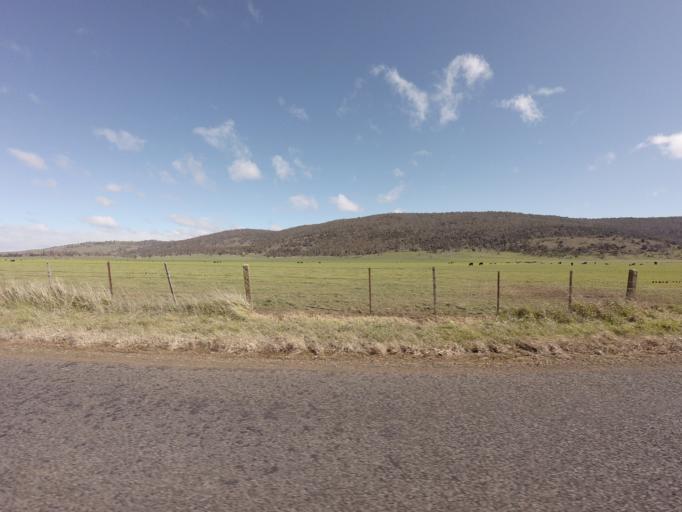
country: AU
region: Tasmania
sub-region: Northern Midlands
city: Evandale
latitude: -41.9750
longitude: 147.4453
